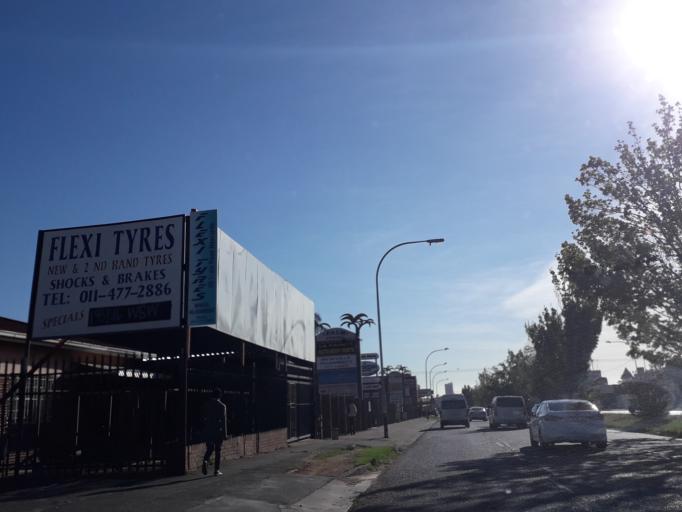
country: ZA
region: Gauteng
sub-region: City of Johannesburg Metropolitan Municipality
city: Roodepoort
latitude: -26.1742
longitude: 27.9558
